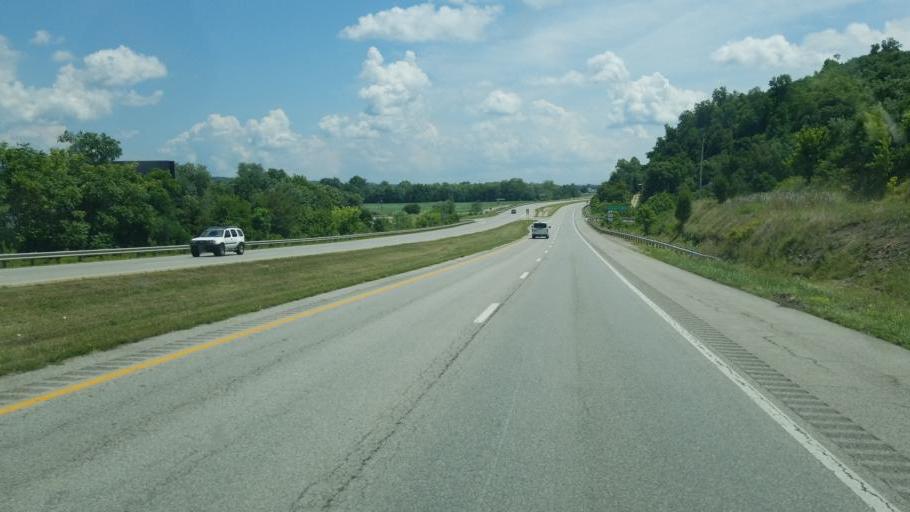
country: US
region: West Virginia
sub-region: Mason County
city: Point Pleasant
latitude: 38.8194
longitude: -82.1197
